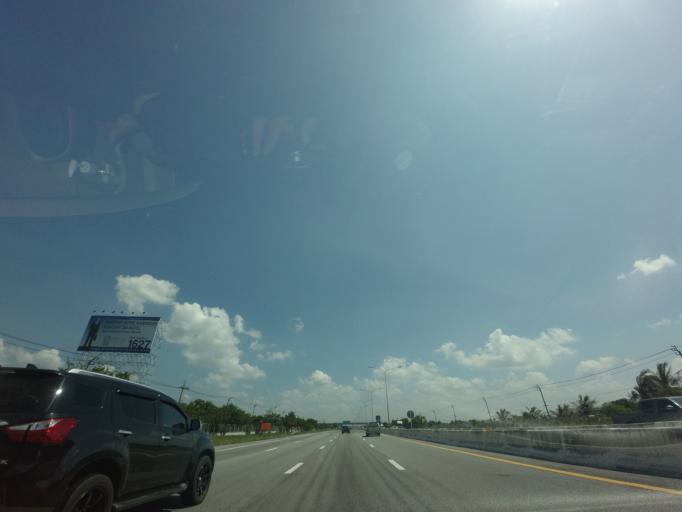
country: TH
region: Samut Prakan
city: Ban Khlong Bang Sao Thong
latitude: 13.6189
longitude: 100.9236
